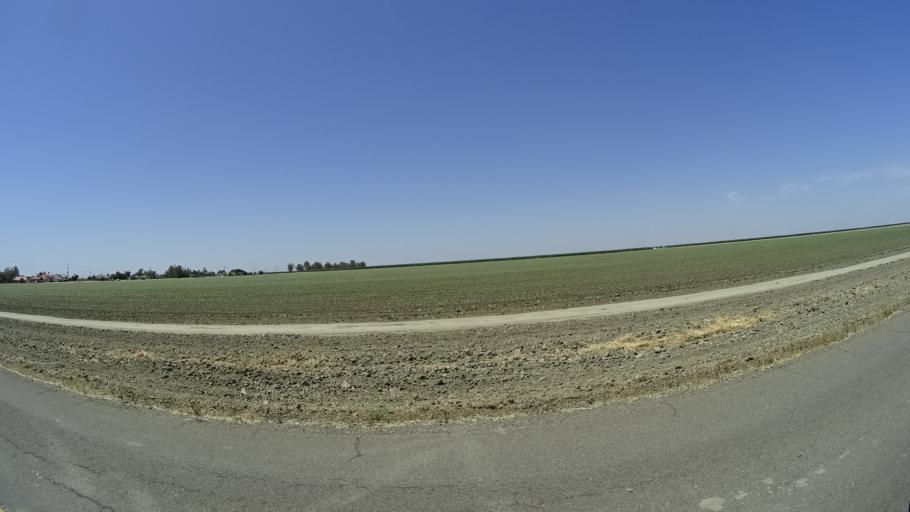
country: US
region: California
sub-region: Kings County
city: Corcoran
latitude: 36.1119
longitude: -119.5808
